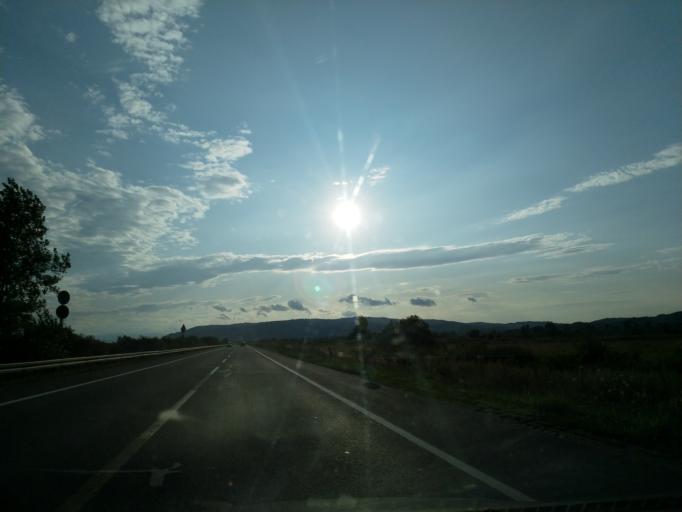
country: RS
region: Central Serbia
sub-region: Rasinski Okrug
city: Krusevac
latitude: 43.6094
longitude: 21.3313
